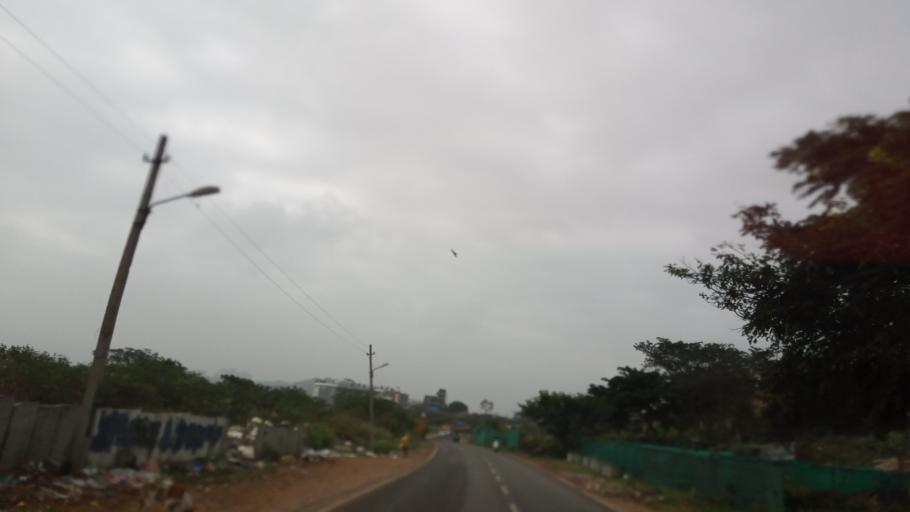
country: IN
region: Karnataka
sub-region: Bangalore Urban
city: Bangalore
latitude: 12.9071
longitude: 77.5334
